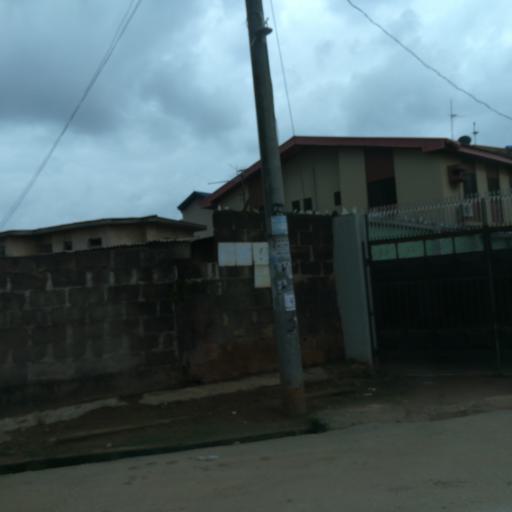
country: NG
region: Lagos
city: Agege
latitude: 6.6085
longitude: 3.2974
